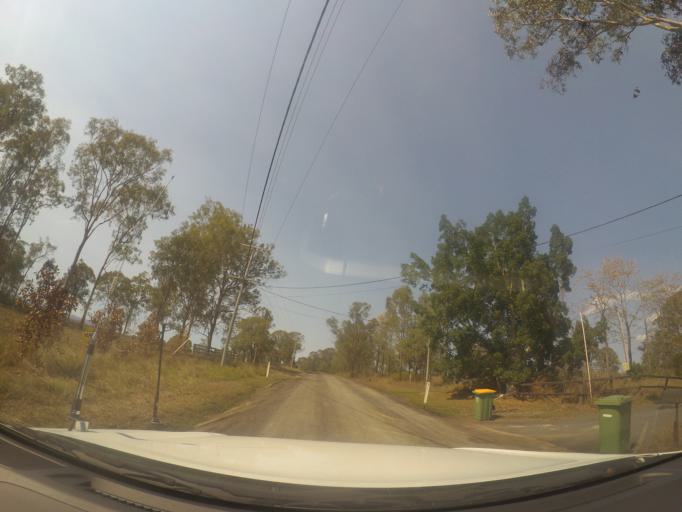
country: AU
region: Queensland
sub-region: Logan
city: Chambers Flat
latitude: -27.7608
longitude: 153.0591
